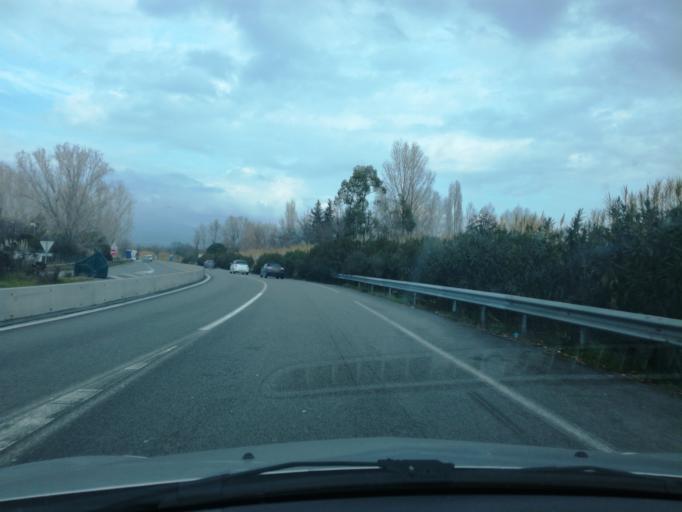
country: FR
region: Provence-Alpes-Cote d'Azur
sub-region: Departement des Alpes-Maritimes
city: Mandelieu-la-Napoule
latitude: 43.5582
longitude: 6.9550
